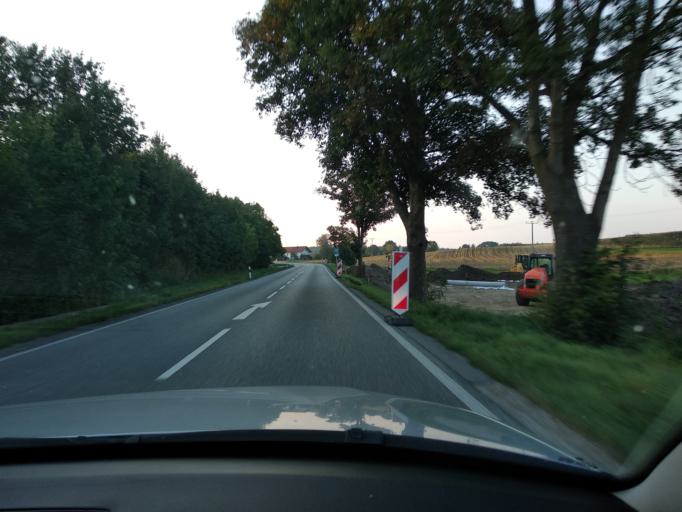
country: DE
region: Bavaria
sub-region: Upper Bavaria
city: Obing
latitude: 48.0103
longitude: 12.3917
